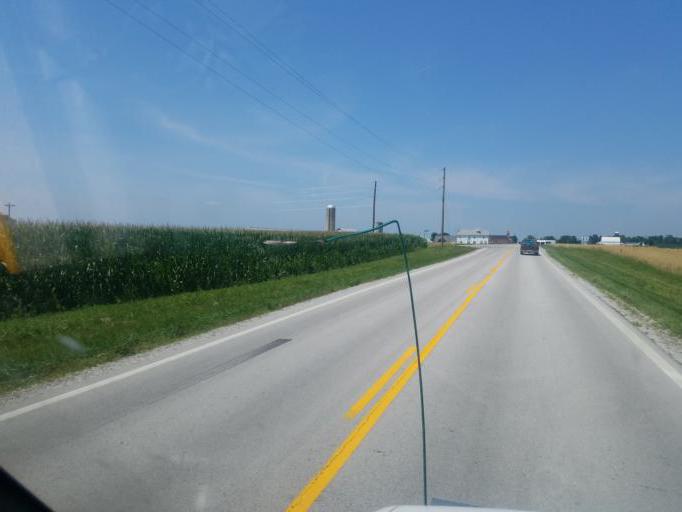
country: US
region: Ohio
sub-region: Auglaize County
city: Minster
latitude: 40.3774
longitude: -84.4340
